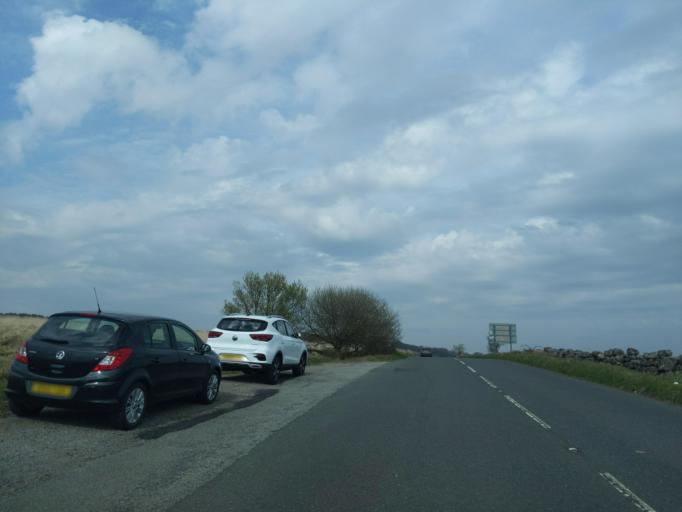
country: GB
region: England
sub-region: Devon
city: Yelverton
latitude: 50.5587
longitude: -3.9619
